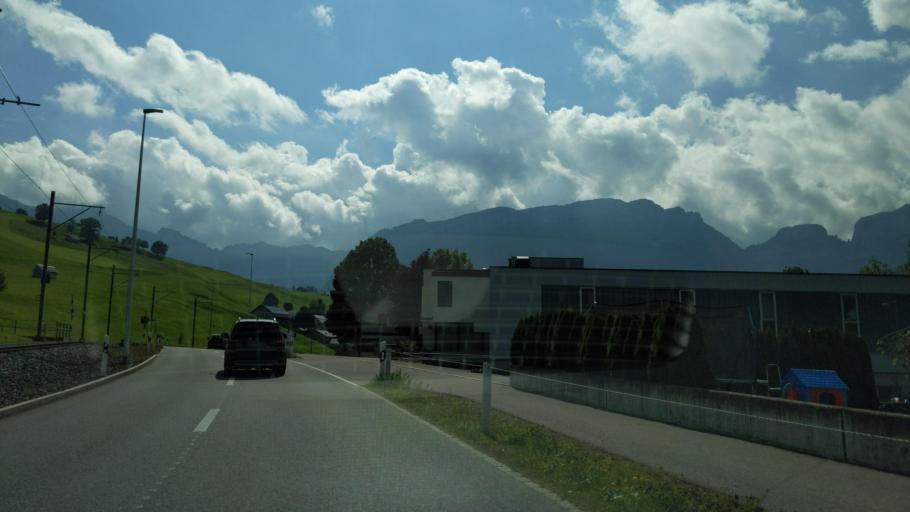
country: CH
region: Appenzell Innerrhoden
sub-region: Appenzell Inner Rhodes
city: Appenzell
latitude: 47.3150
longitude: 9.4345
